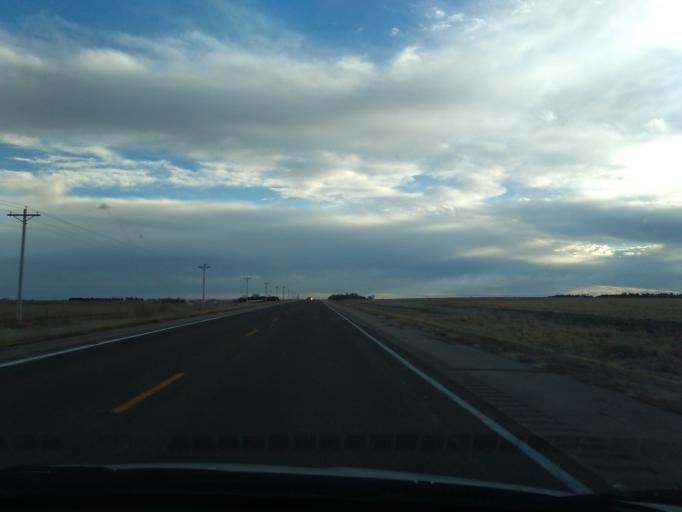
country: US
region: Nebraska
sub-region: Phelps County
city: Holdrege
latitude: 40.3761
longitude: -99.3700
